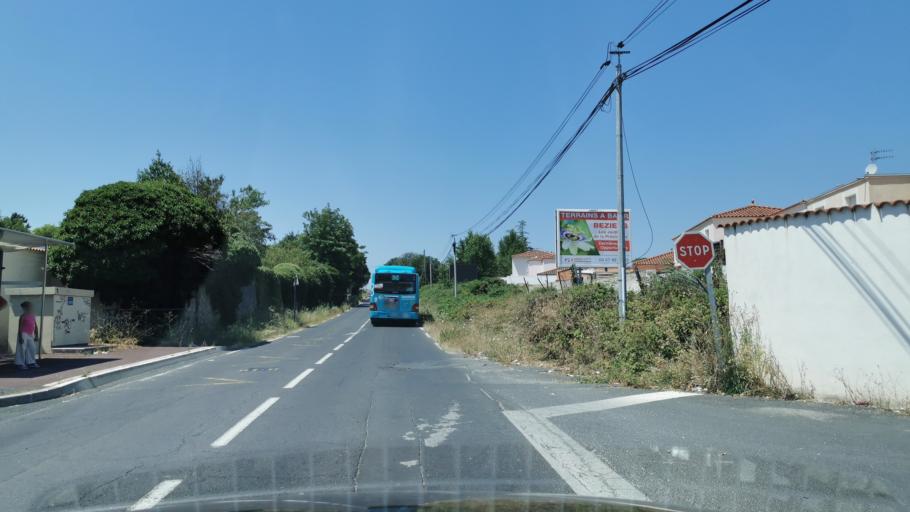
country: FR
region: Languedoc-Roussillon
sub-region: Departement de l'Herault
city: Beziers
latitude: 43.3410
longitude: 3.1869
